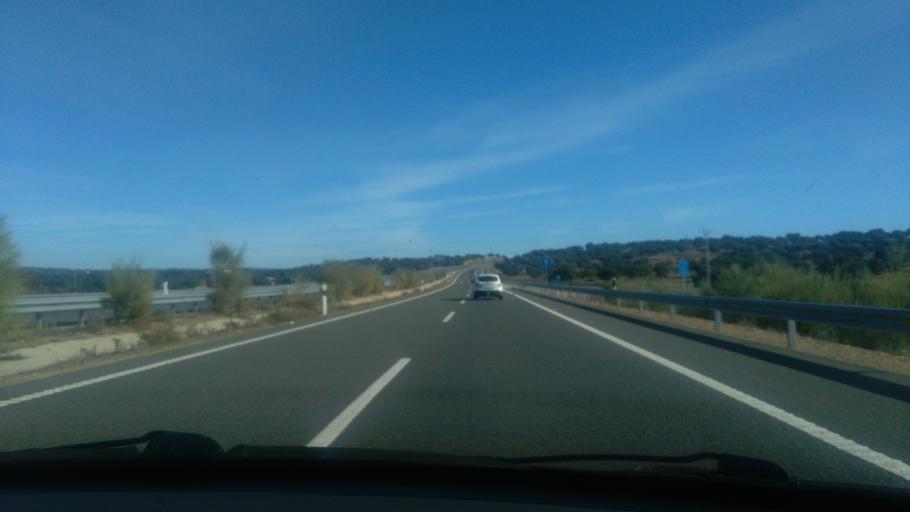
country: ES
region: Extremadura
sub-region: Provincia de Caceres
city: Plasenzuela
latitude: 39.4411
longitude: -6.0565
